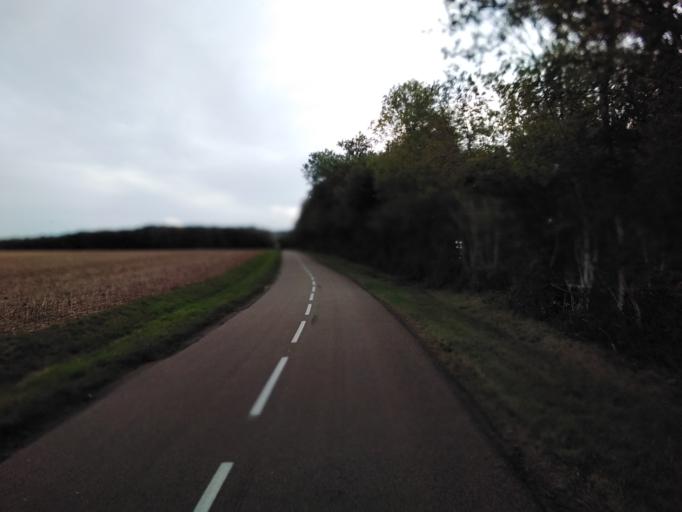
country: FR
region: Bourgogne
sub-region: Departement de l'Yonne
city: Ravieres
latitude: 47.8048
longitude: 4.3574
